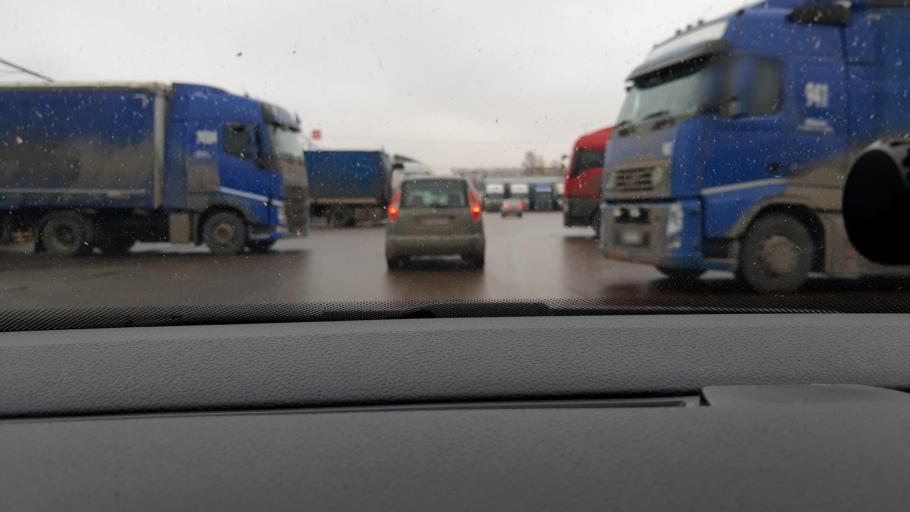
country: RU
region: Moscow
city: Ryazanskiy
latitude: 55.7187
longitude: 37.7606
